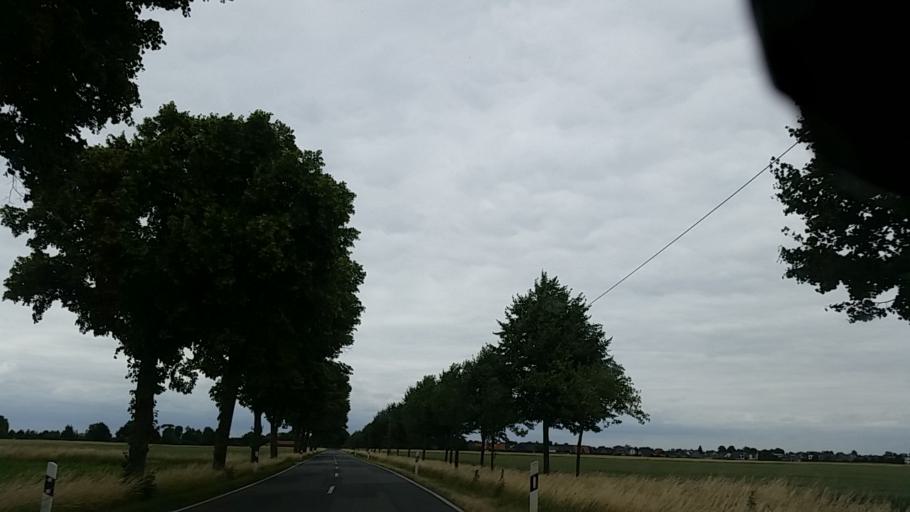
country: DE
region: Lower Saxony
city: Grafhorst
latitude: 52.4373
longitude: 10.9345
